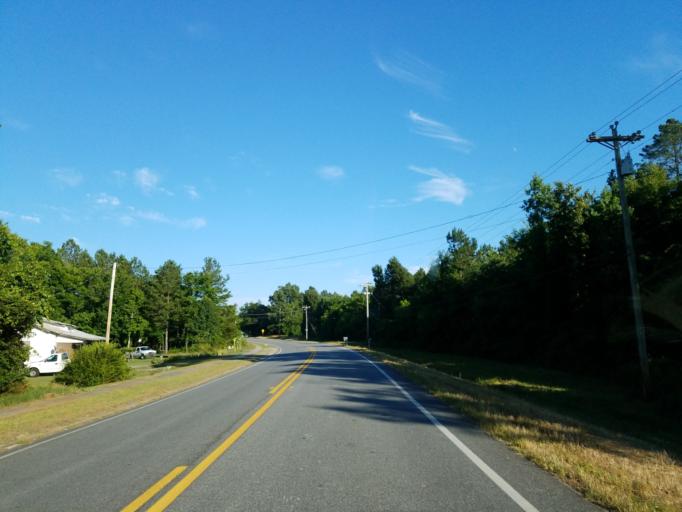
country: US
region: Georgia
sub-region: Gordon County
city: Calhoun
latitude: 34.5604
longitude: -85.0172
